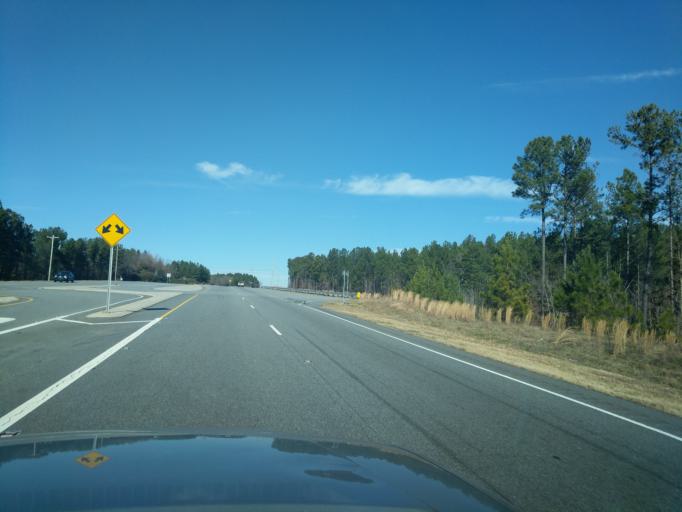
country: US
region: North Carolina
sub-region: Rutherford County
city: Forest City
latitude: 35.2101
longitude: -81.8390
